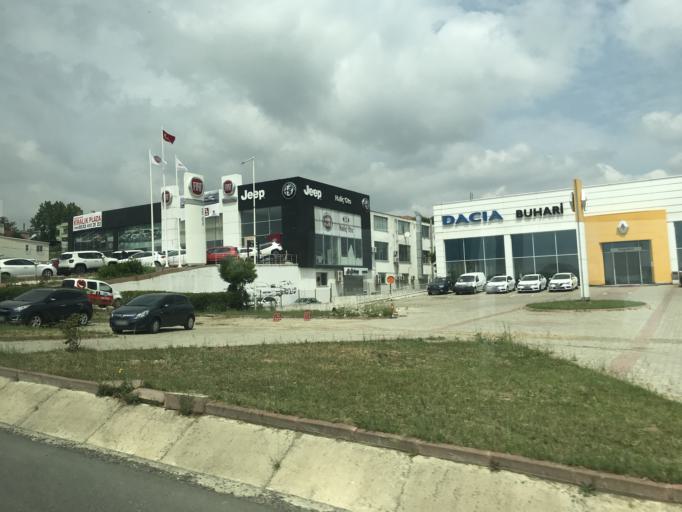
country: TR
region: Tekirdag
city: Tekirdag
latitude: 40.9879
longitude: 27.5948
